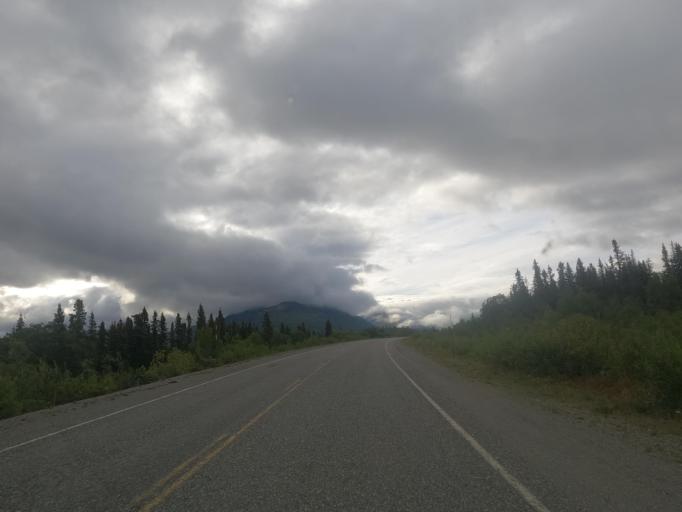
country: CA
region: Yukon
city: Haines Junction
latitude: 59.9782
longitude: -136.8223
